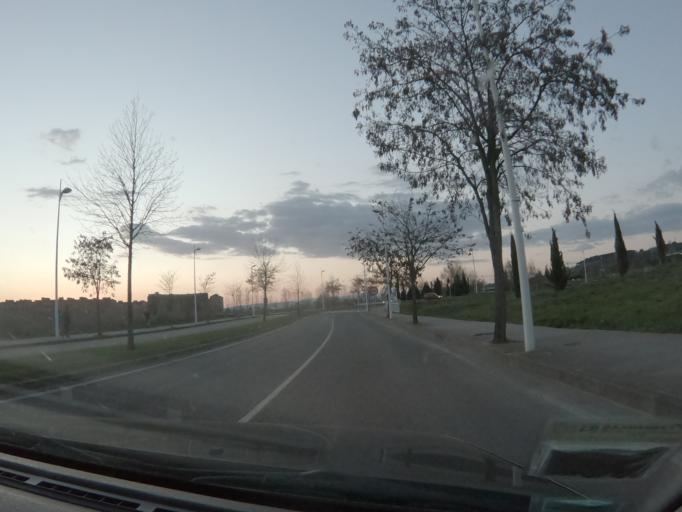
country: ES
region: Castille and Leon
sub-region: Provincia de Leon
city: Ponferrada
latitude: 42.5543
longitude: -6.5879
